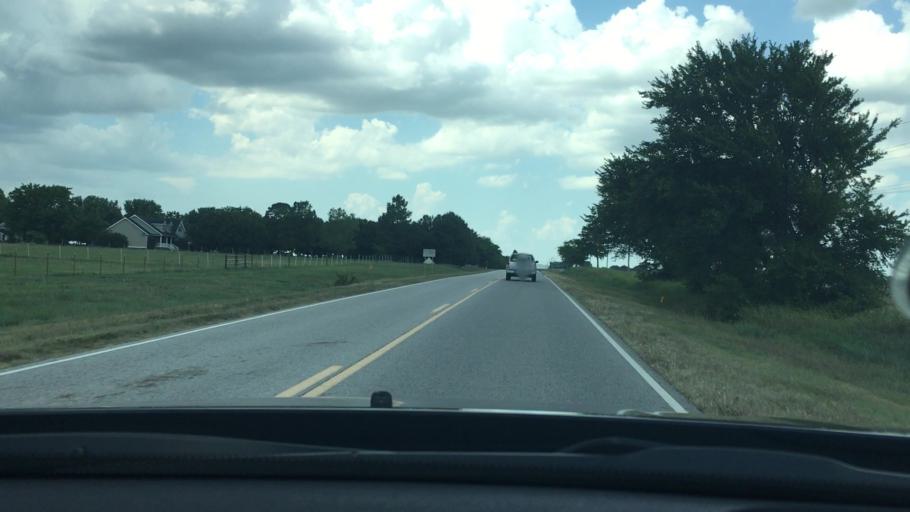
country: US
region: Oklahoma
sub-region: Pontotoc County
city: Ada
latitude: 34.6628
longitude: -96.6349
